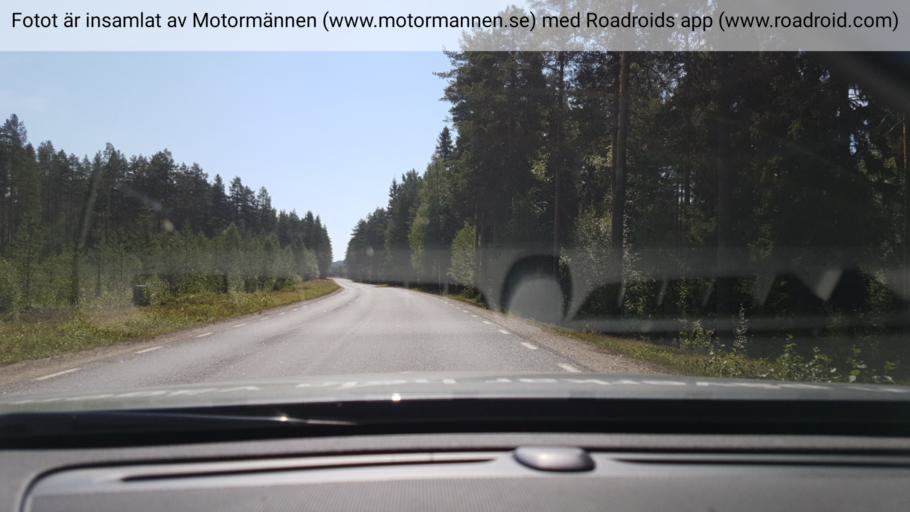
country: SE
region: Vaesterbotten
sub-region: Vindelns Kommun
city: Vindeln
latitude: 64.2837
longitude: 19.6203
